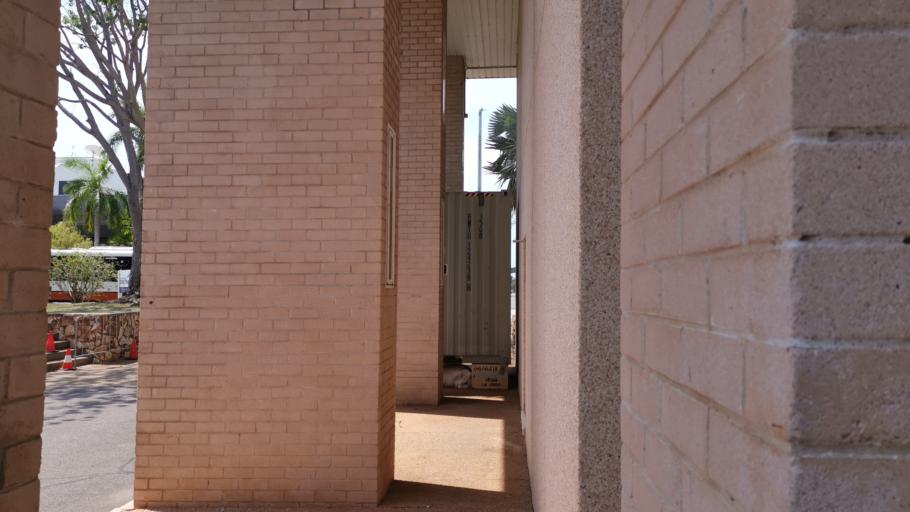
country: AU
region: Northern Territory
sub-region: Darwin
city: Darwin
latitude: -12.4647
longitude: 130.8452
